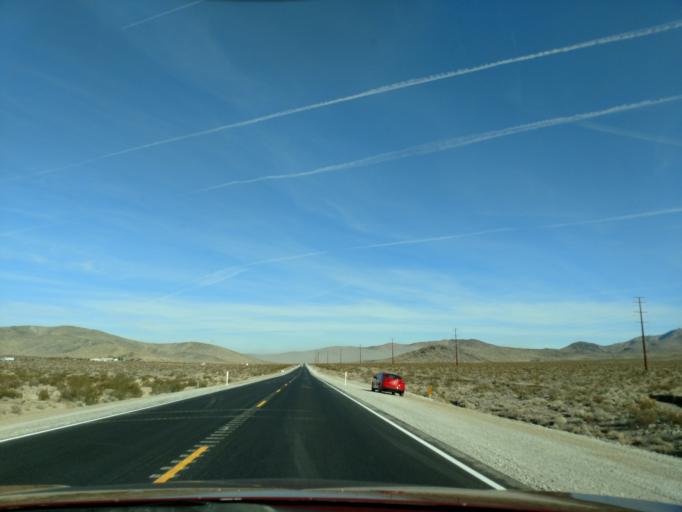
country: US
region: Nevada
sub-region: Nye County
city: Pahrump
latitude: 36.4142
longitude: -116.0693
